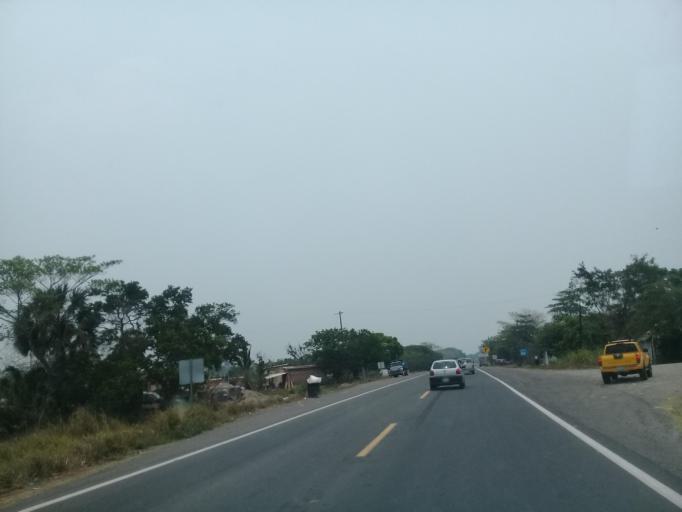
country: MX
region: Veracruz
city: Paso del Toro
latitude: 18.9808
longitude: -96.1747
